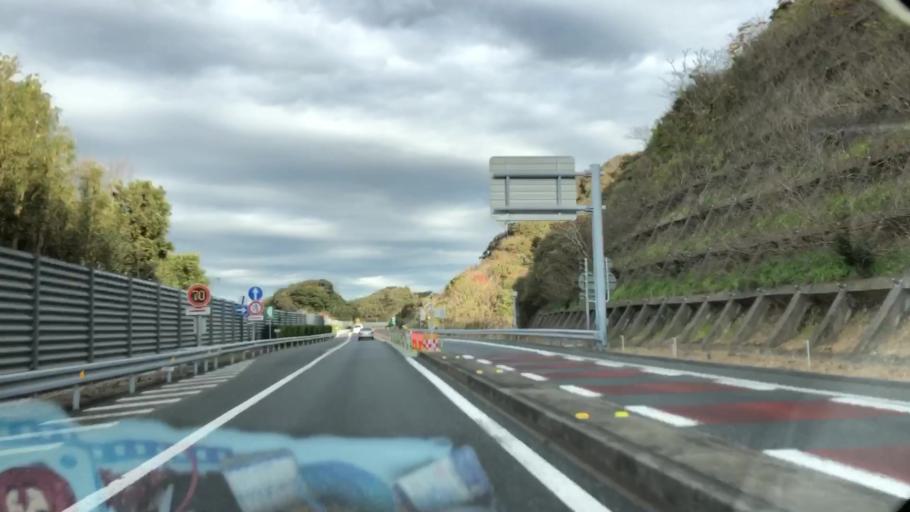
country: JP
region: Chiba
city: Tateyama
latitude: 35.0456
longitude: 139.8531
